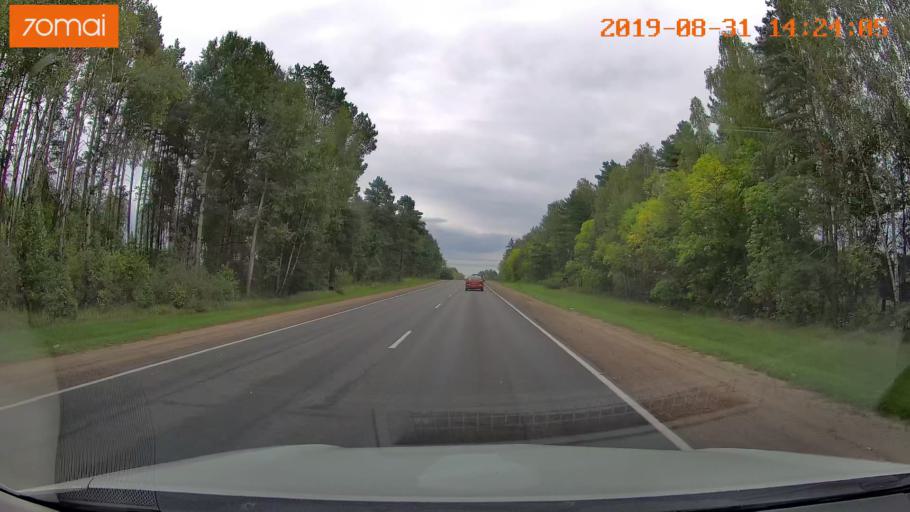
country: RU
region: Smolensk
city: Yekimovichi
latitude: 54.1007
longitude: 33.2479
